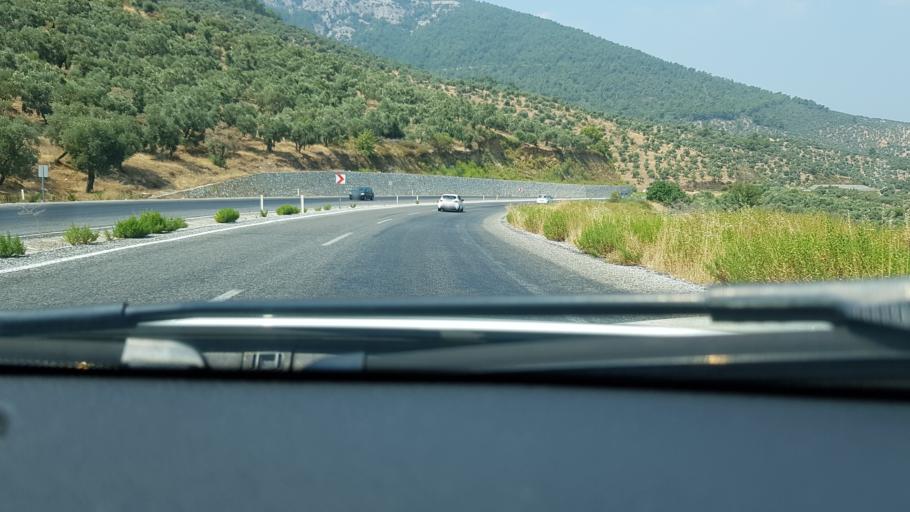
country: TR
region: Aydin
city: Sarikemer
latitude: 37.4636
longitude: 27.4967
